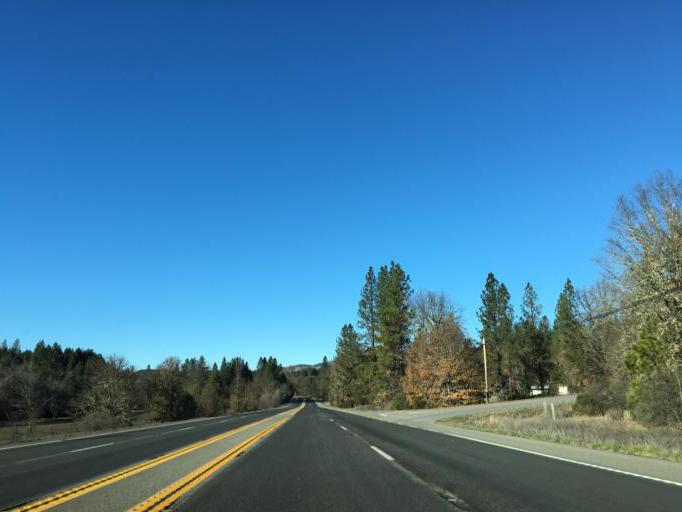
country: US
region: California
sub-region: Mendocino County
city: Laytonville
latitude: 39.7213
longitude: -123.5017
